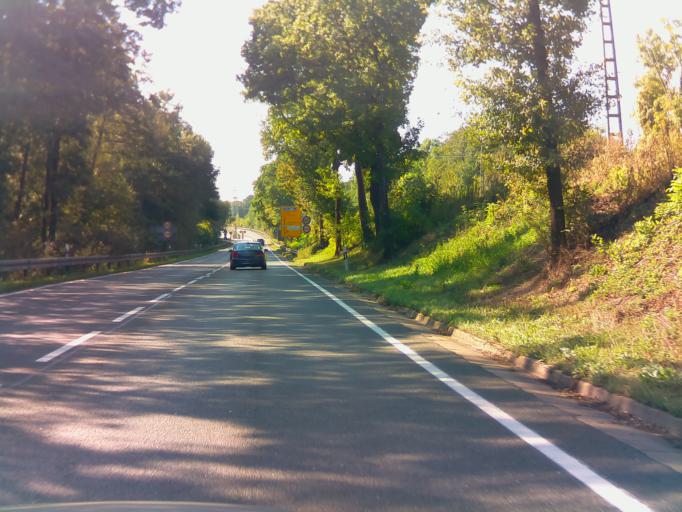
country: DE
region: Bavaria
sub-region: Upper Franconia
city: Michelau
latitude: 50.1527
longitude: 11.0986
